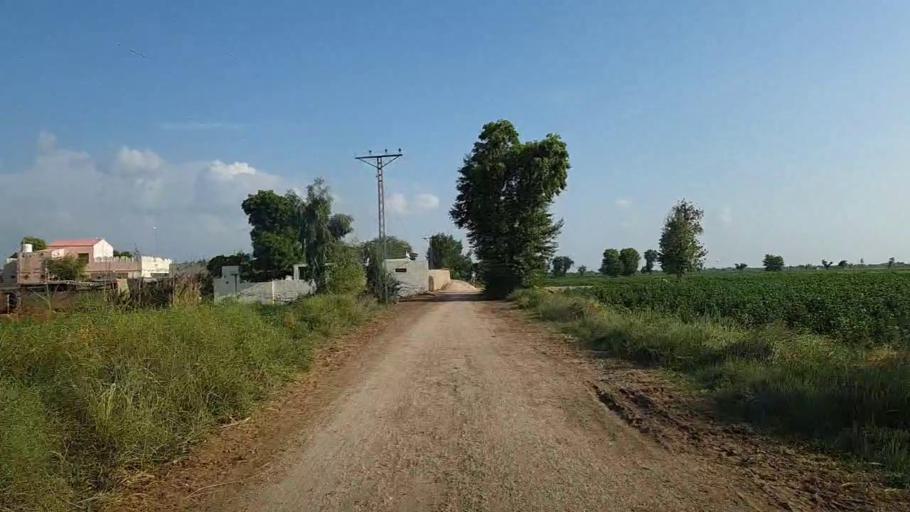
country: PK
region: Sindh
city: Hingorja
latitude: 27.0926
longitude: 68.3648
